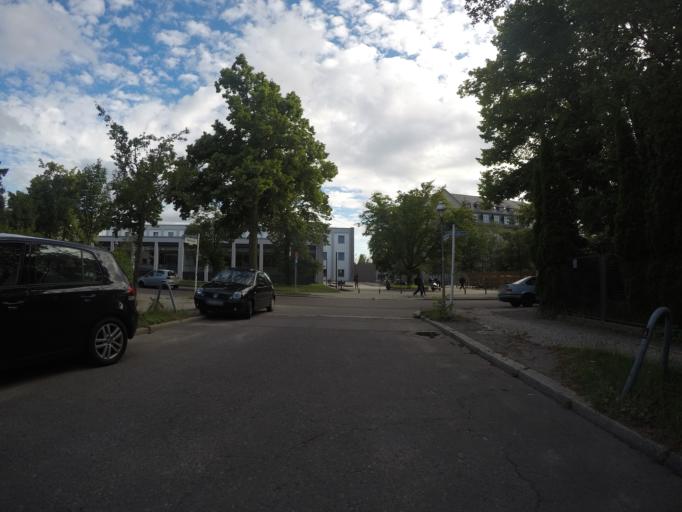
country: DE
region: Berlin
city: Dahlem
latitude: 52.4485
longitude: 13.2816
